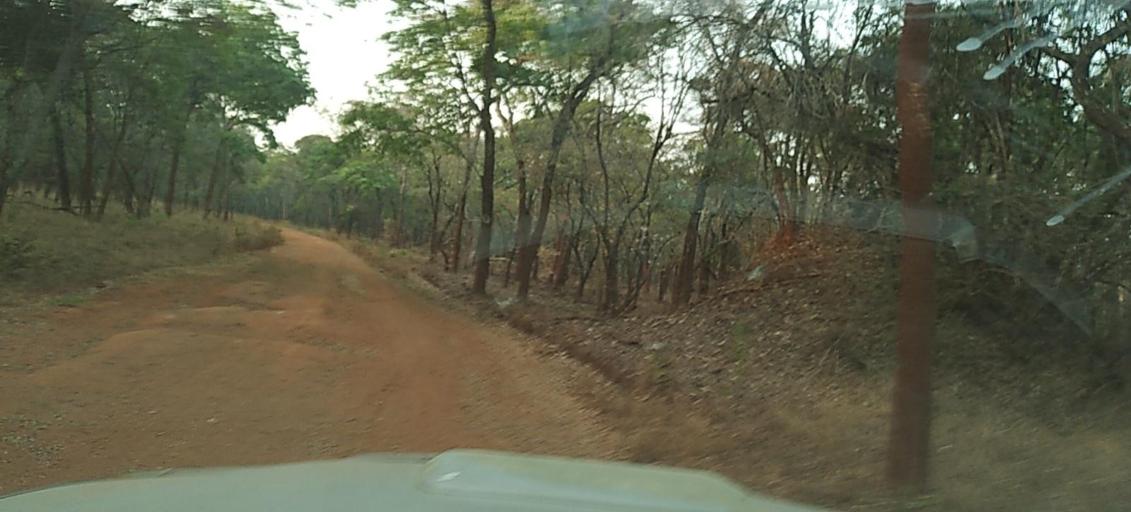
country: ZM
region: North-Western
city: Kasempa
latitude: -13.1058
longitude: 26.4052
